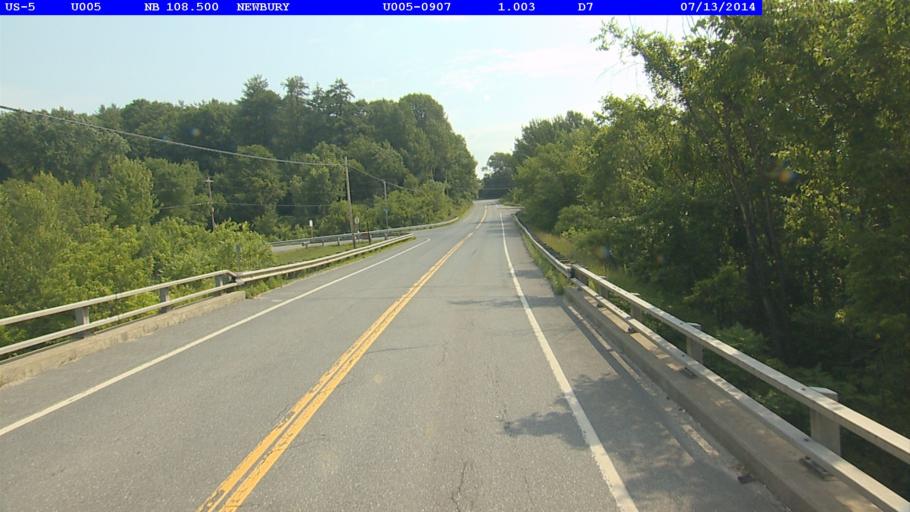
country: US
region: New Hampshire
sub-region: Grafton County
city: Haverhill
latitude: 44.0458
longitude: -72.0814
